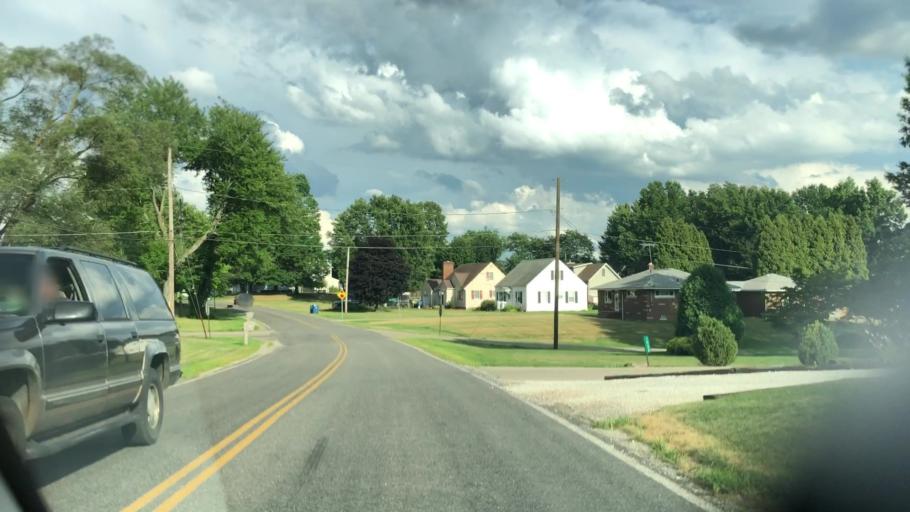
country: US
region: Ohio
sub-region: Summit County
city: Norton
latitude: 41.0214
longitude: -81.6270
